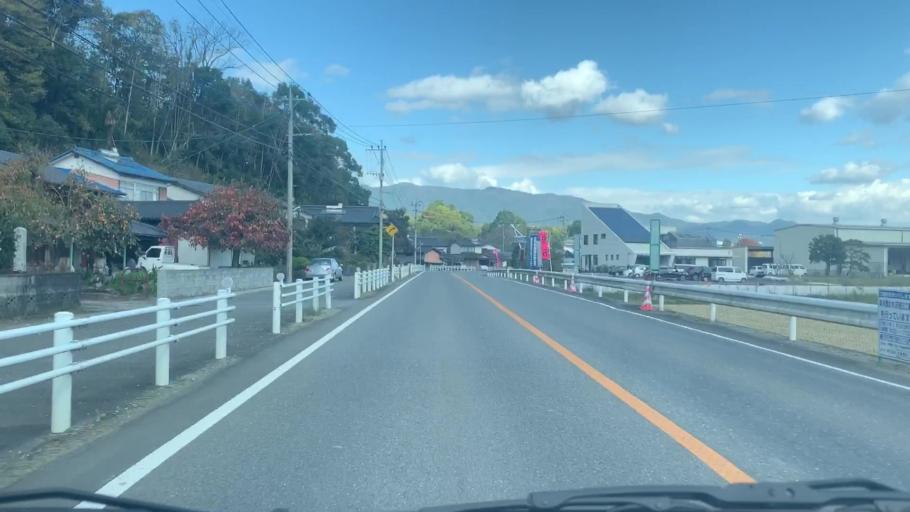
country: JP
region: Saga Prefecture
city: Saga-shi
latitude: 33.2694
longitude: 130.1806
